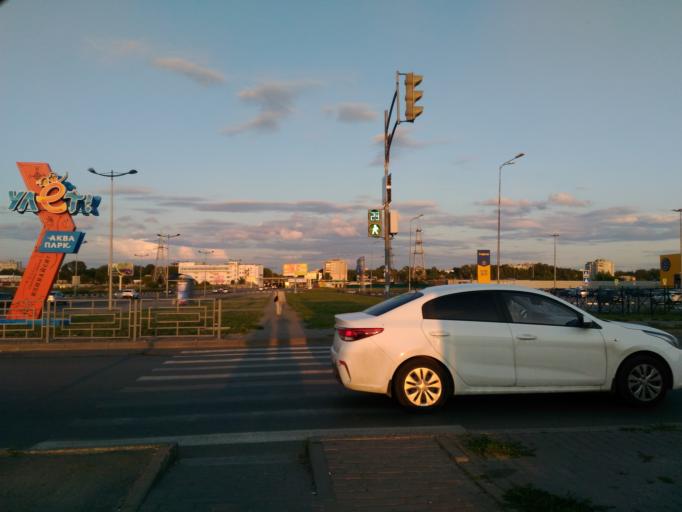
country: RU
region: Ulyanovsk
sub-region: Ulyanovskiy Rayon
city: Ulyanovsk
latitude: 54.2878
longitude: 48.2781
